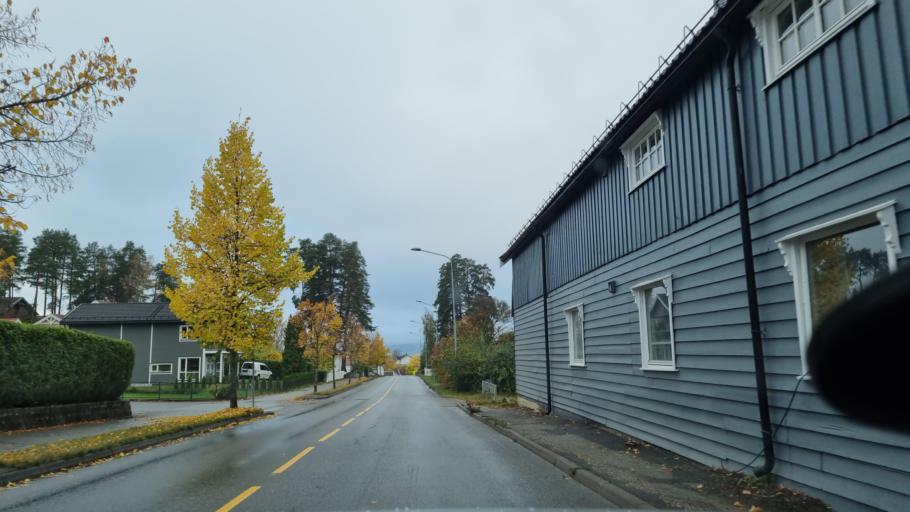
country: NO
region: Hedmark
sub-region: Hamar
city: Hamar
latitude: 60.8010
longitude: 11.0617
